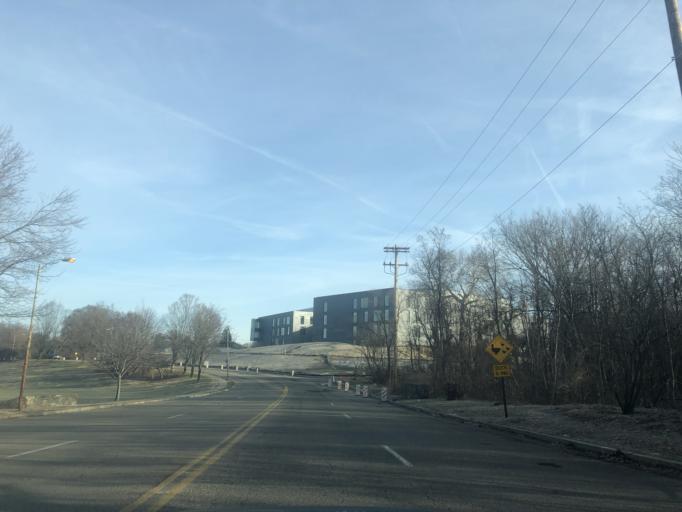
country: US
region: Pennsylvania
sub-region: Delaware County
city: Radnor
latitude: 40.0377
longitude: -75.3559
